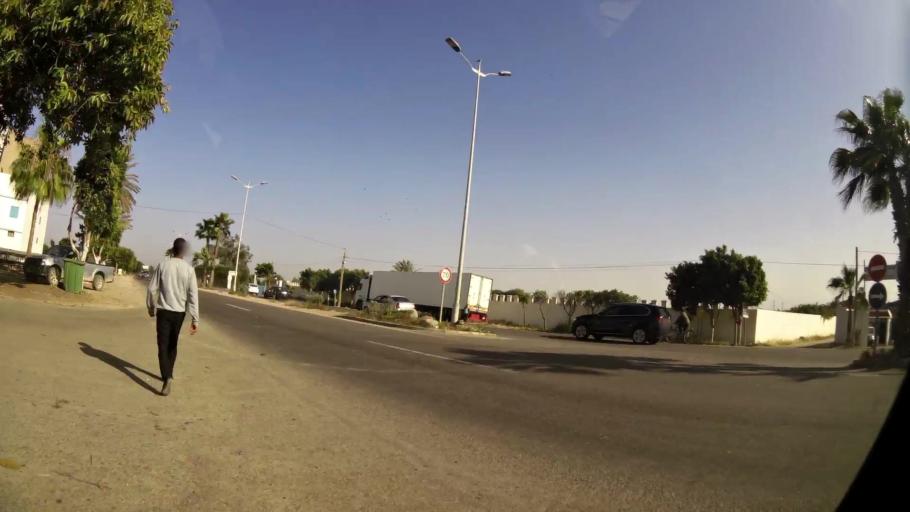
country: MA
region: Souss-Massa-Draa
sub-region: Inezgane-Ait Mellou
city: Inezgane
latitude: 30.3709
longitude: -9.5031
